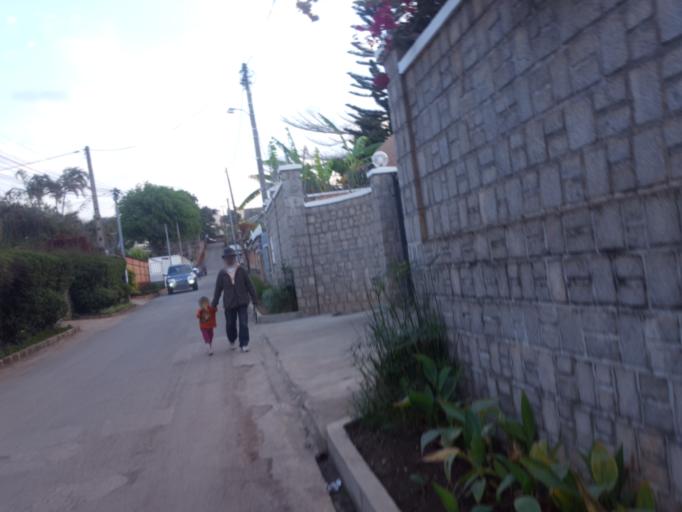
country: MG
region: Analamanga
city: Antananarivo
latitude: -18.8685
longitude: 47.5339
